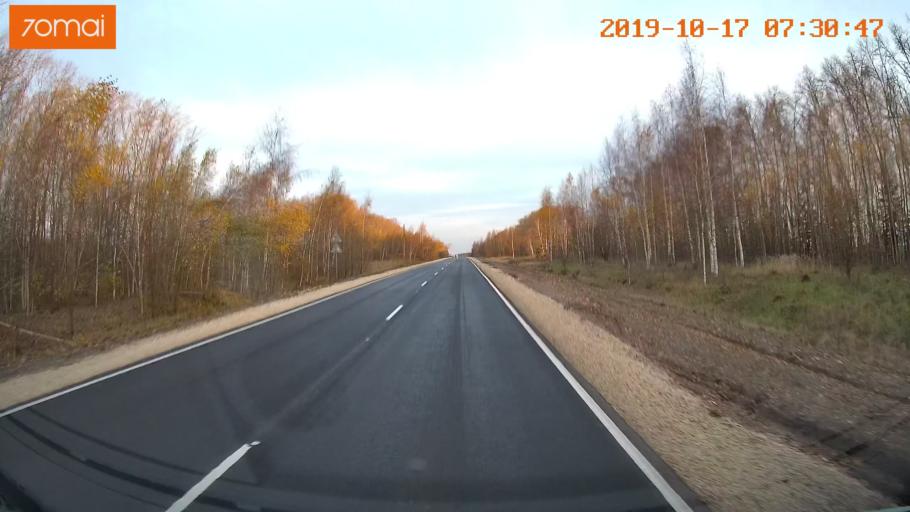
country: RU
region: Ivanovo
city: Gavrilov Posad
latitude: 56.3808
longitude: 40.0057
